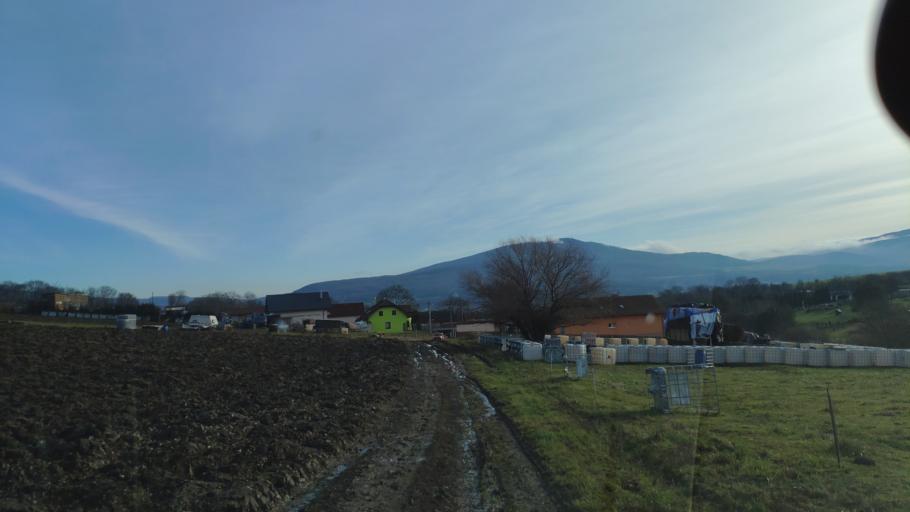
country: SK
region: Kosicky
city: Kosice
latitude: 48.6867
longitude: 21.3928
